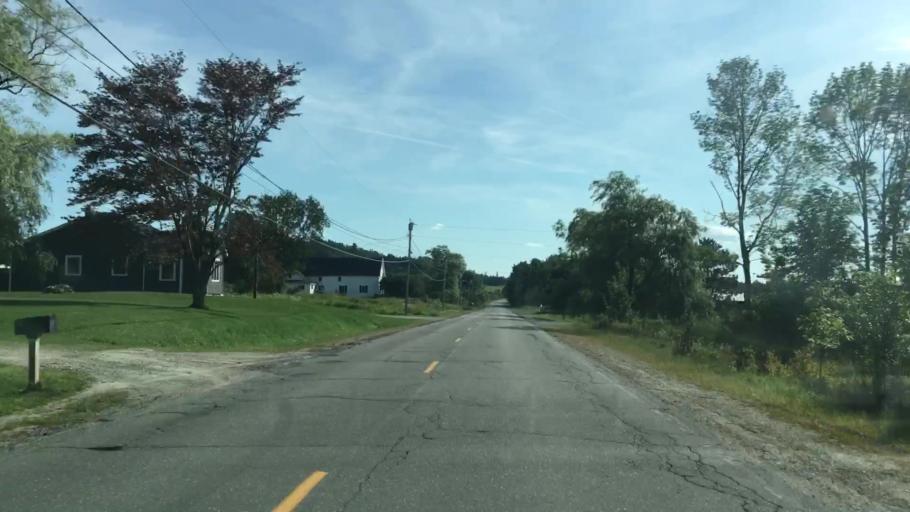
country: US
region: Maine
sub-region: Penobscot County
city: Lincoln
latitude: 45.3263
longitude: -68.5319
